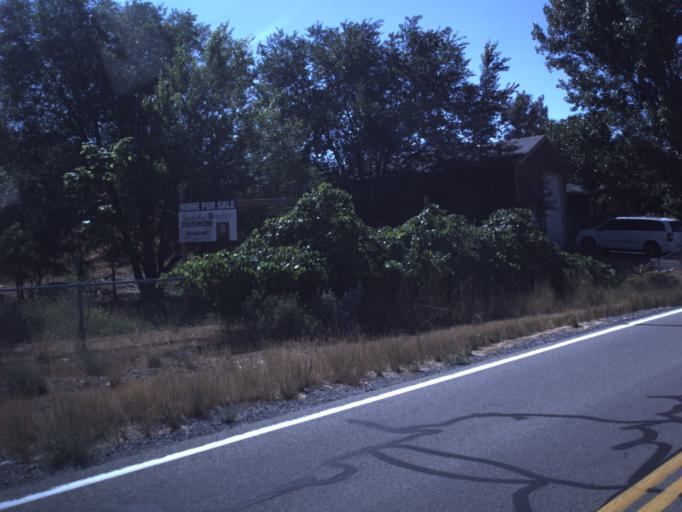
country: US
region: Utah
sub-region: Tooele County
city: Tooele
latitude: 40.4488
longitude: -112.3635
